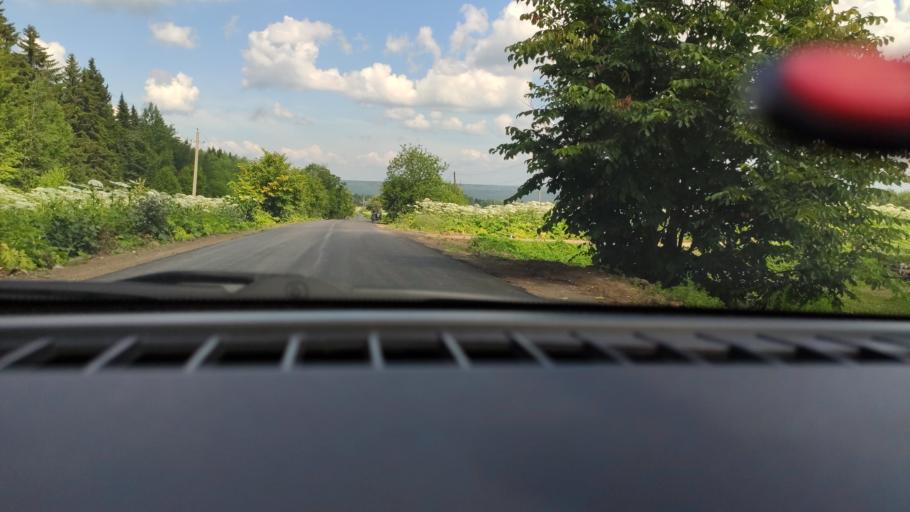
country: RU
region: Perm
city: Sylva
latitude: 58.0345
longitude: 56.7233
